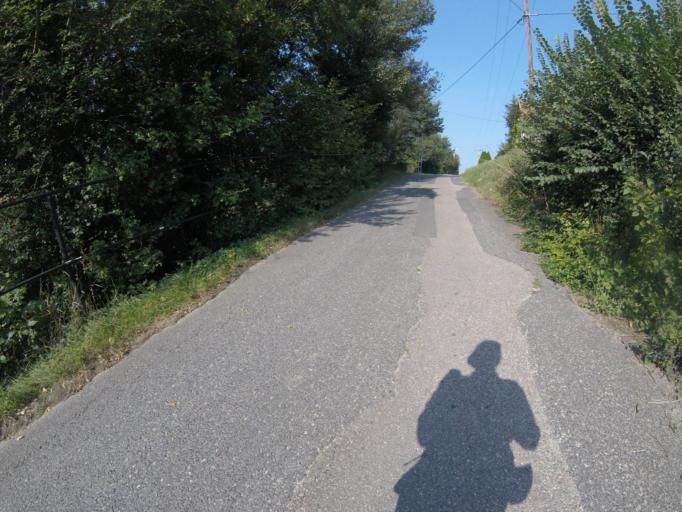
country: HU
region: Gyor-Moson-Sopron
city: Fertorakos
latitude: 47.7239
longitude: 16.6381
